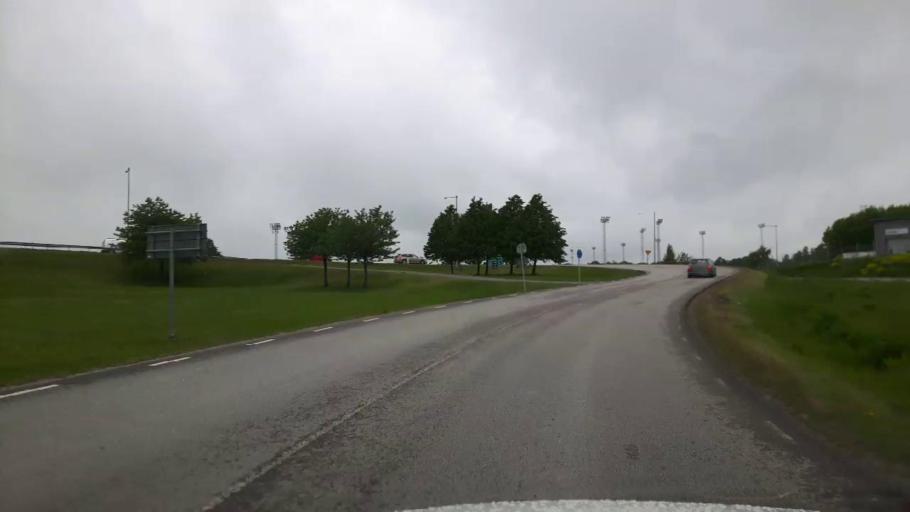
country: SE
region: Stockholm
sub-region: Upplands-Bro Kommun
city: Bro
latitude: 59.5173
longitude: 17.6182
